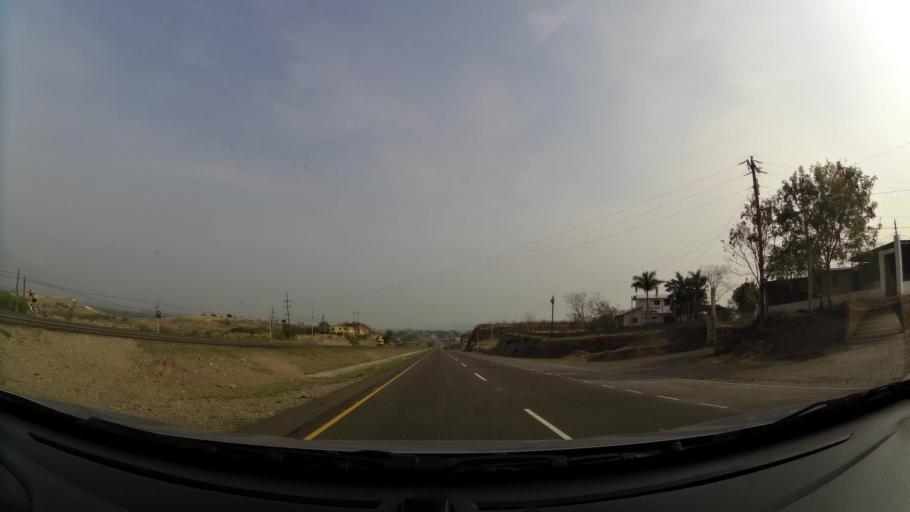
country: HN
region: Comayagua
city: Comayagua
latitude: 14.4071
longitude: -87.6209
